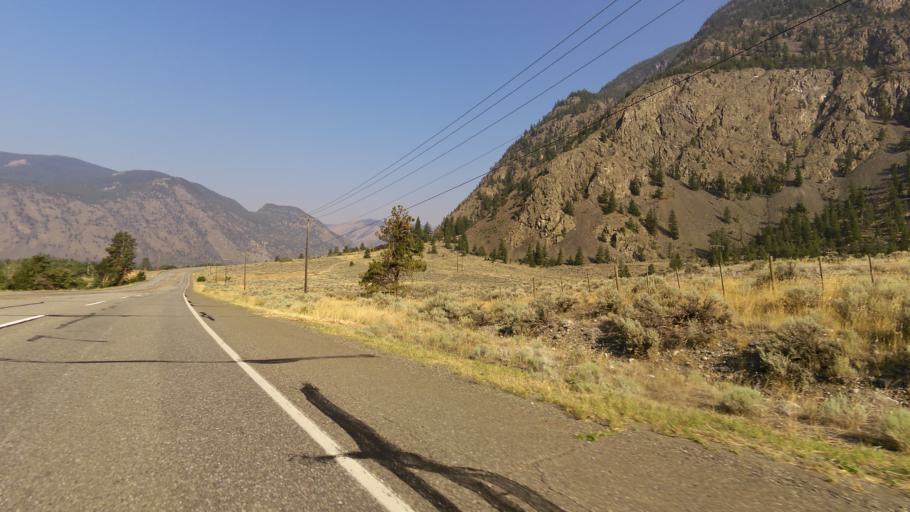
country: CA
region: British Columbia
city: Oliver
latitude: 49.2203
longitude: -119.9481
